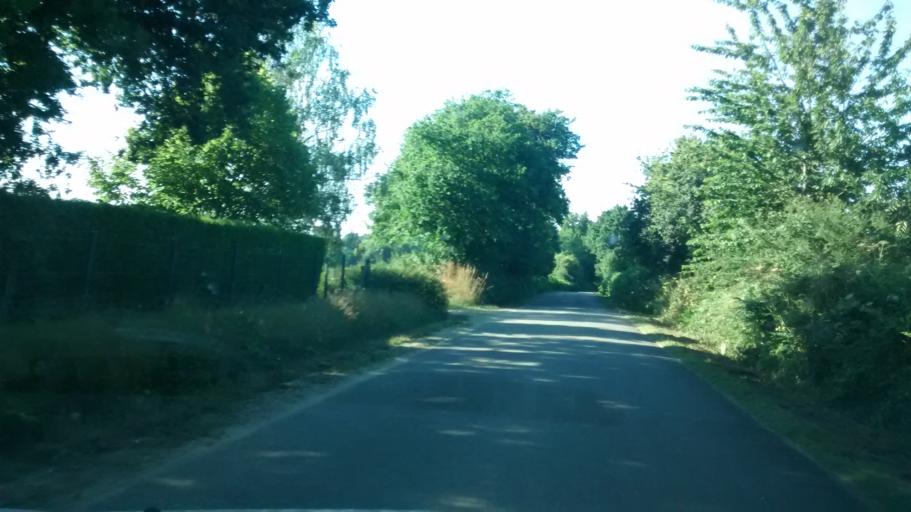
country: FR
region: Brittany
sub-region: Departement du Morbihan
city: Molac
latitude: 47.7867
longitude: -2.4386
